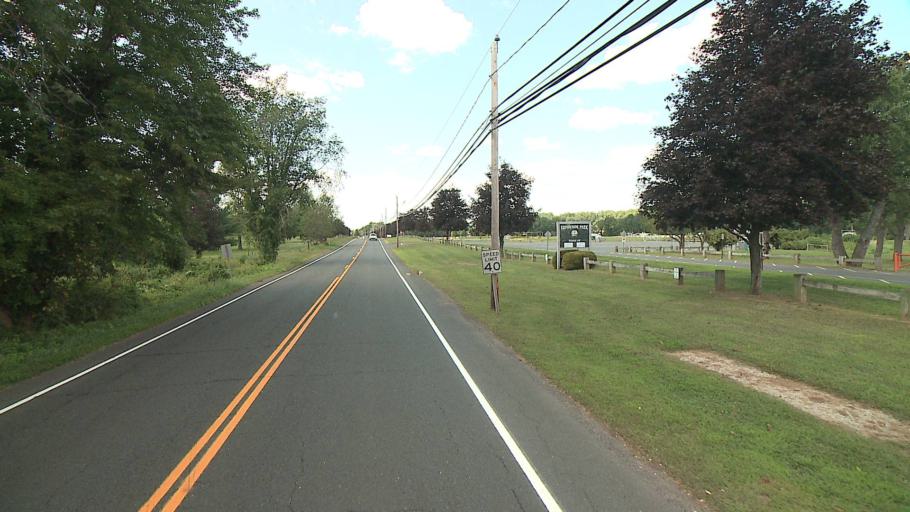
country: US
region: Connecticut
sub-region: Tolland County
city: Ellington
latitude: 41.9123
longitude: -72.4877
